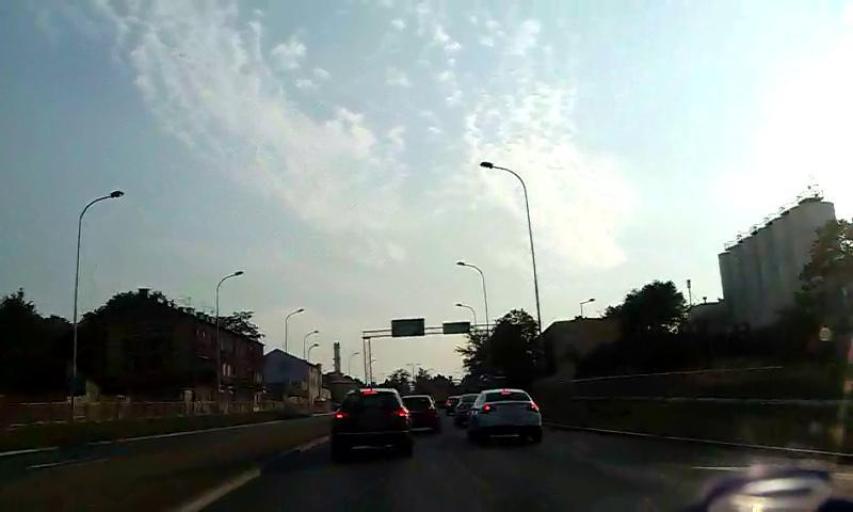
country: PL
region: Lublin Voivodeship
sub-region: Powiat lubelski
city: Lublin
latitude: 51.2243
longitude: 22.5783
